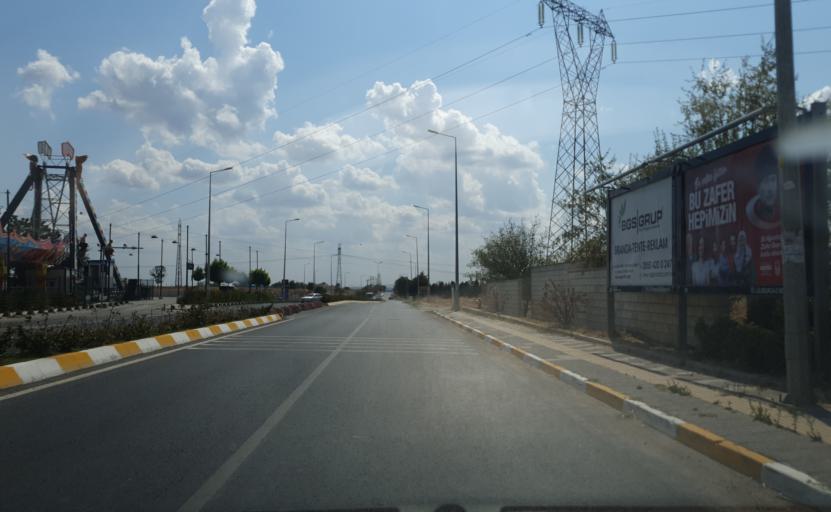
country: TR
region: Kirklareli
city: Luleburgaz
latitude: 41.3859
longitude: 27.3473
